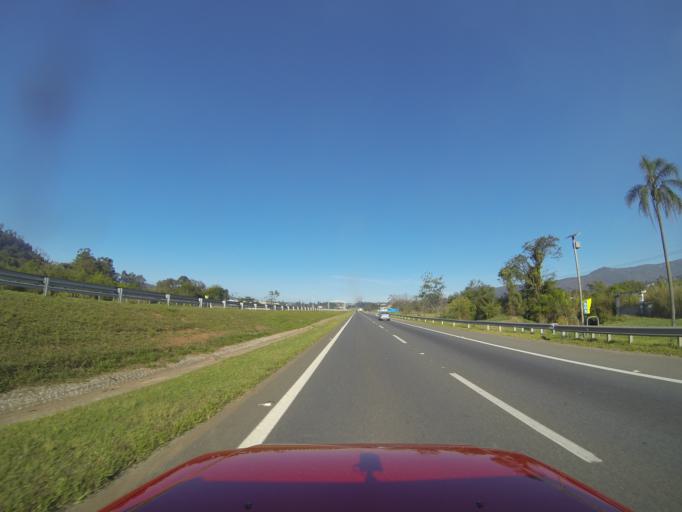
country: BR
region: Sao Paulo
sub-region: Atibaia
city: Atibaia
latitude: -23.1073
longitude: -46.5322
